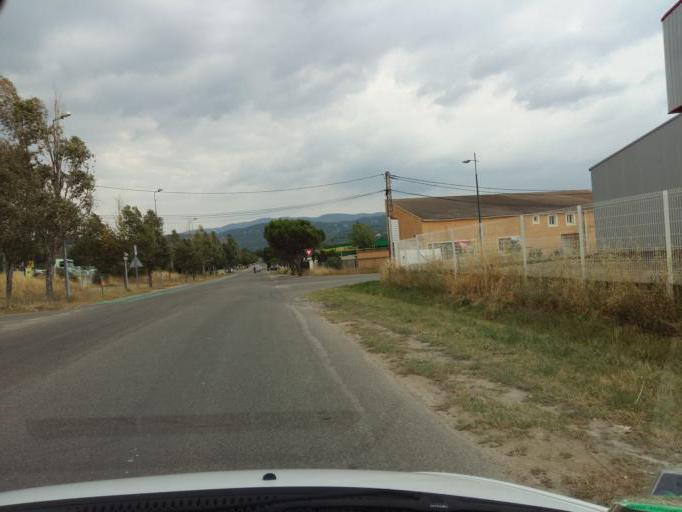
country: FR
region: Provence-Alpes-Cote d'Azur
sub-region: Departement du Vaucluse
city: Gargas
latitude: 43.8903
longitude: 5.3721
